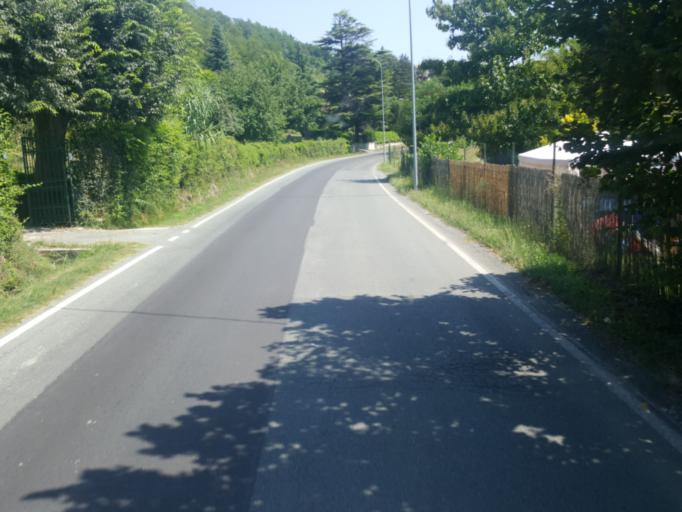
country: IT
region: Piedmont
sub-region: Provincia di Alessandria
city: Acqui Terme
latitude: 44.6798
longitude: 8.4843
